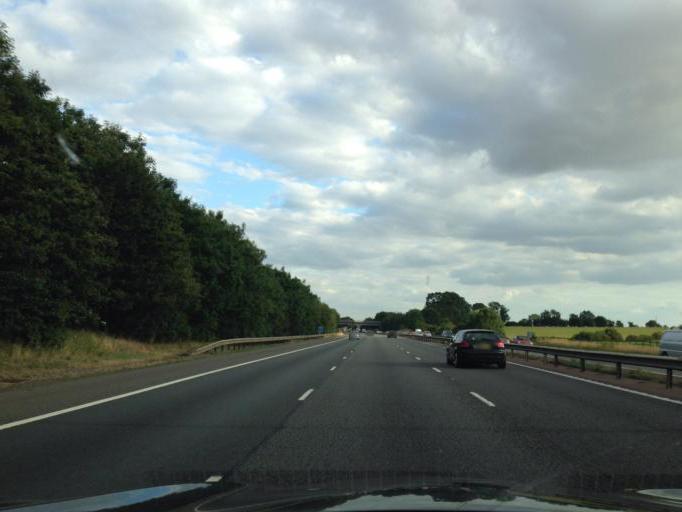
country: GB
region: England
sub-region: Oxfordshire
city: Adderbury
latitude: 52.0286
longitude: -1.2984
